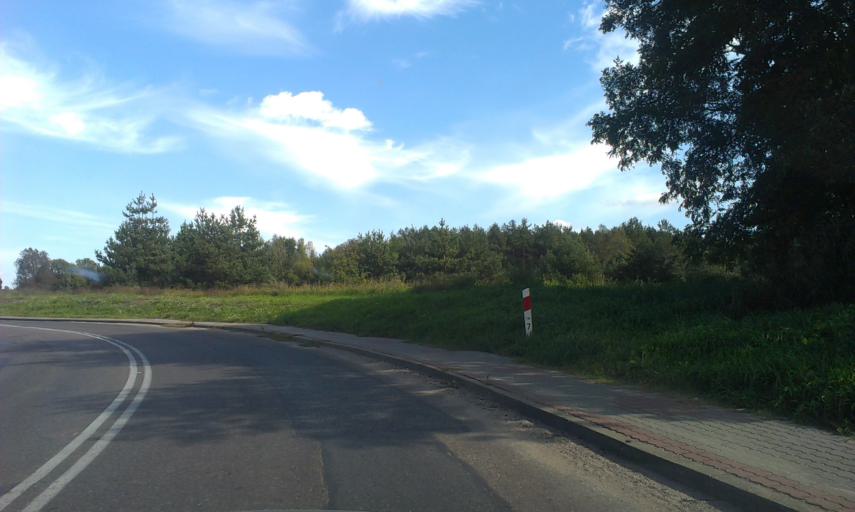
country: PL
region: Greater Poland Voivodeship
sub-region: Powiat zlotowski
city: Zlotow
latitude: 53.3525
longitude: 17.0494
